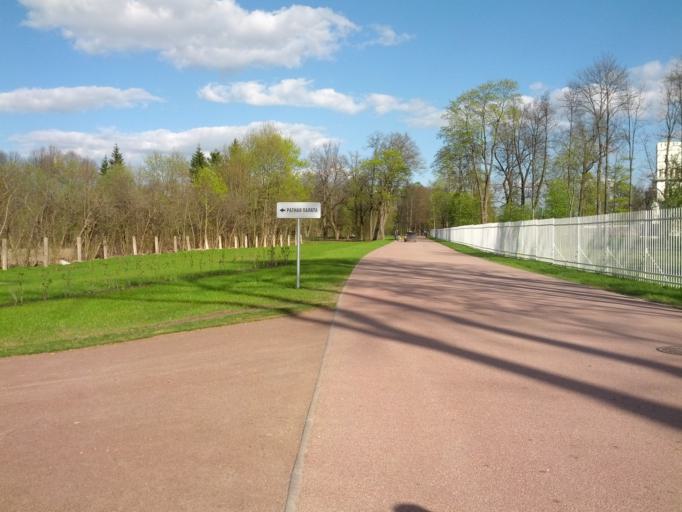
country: RU
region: St.-Petersburg
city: Pushkin
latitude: 59.7249
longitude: 30.3865
